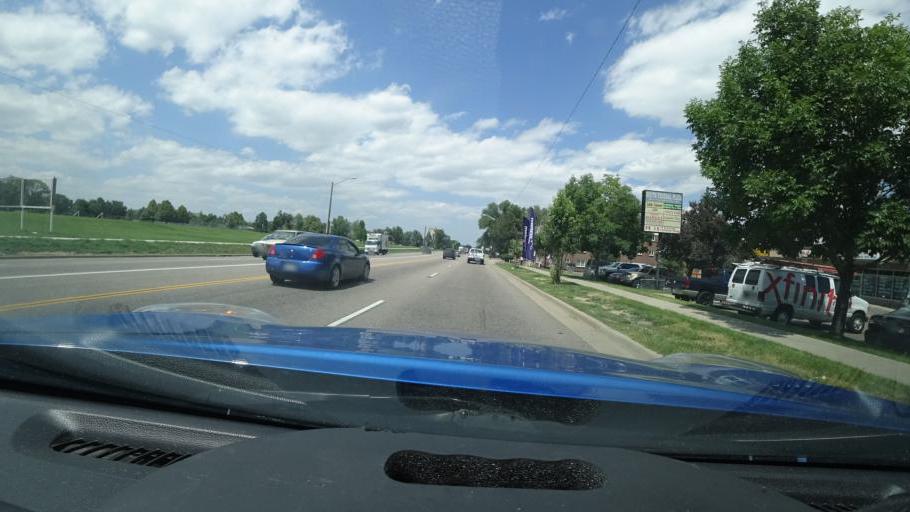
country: US
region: Colorado
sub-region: Arapahoe County
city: Sheridan
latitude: 39.6623
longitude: -105.0251
